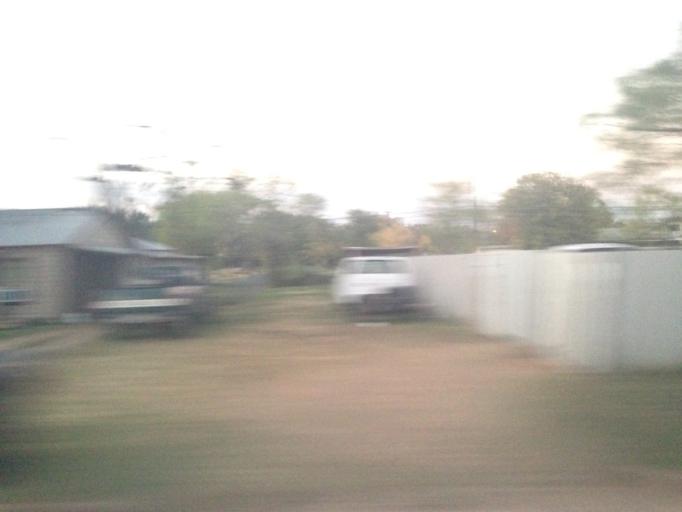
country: US
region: Texas
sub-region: Taylor County
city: Abilene
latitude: 32.4474
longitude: -99.7549
